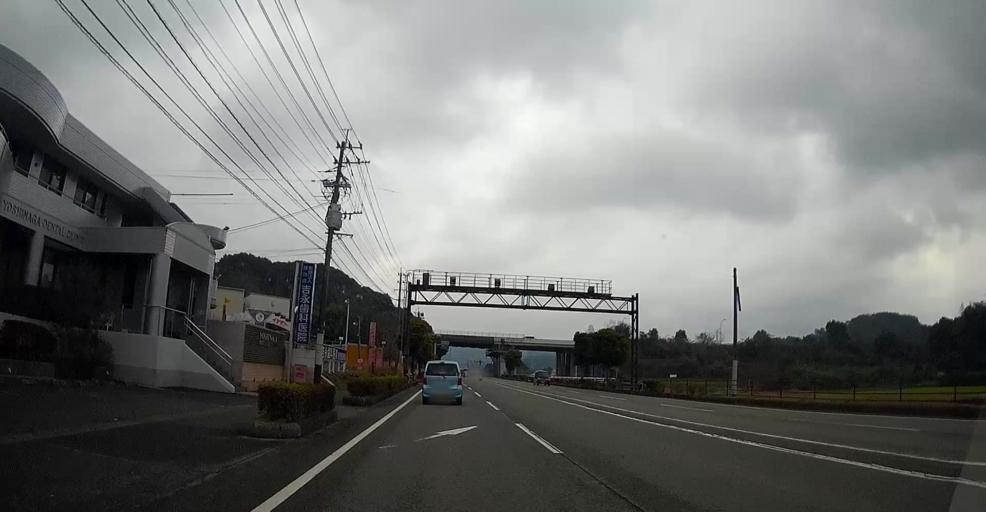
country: JP
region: Kumamoto
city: Matsubase
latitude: 32.6510
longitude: 130.7080
